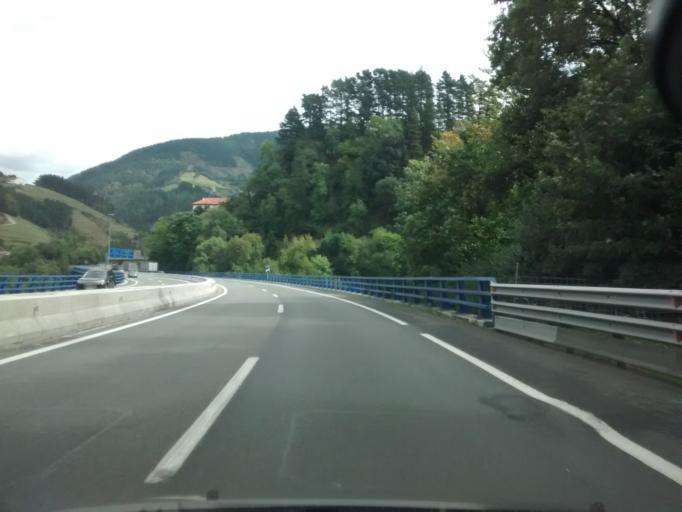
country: ES
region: Basque Country
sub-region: Provincia de Guipuzcoa
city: Eibar
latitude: 43.1888
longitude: -2.4525
